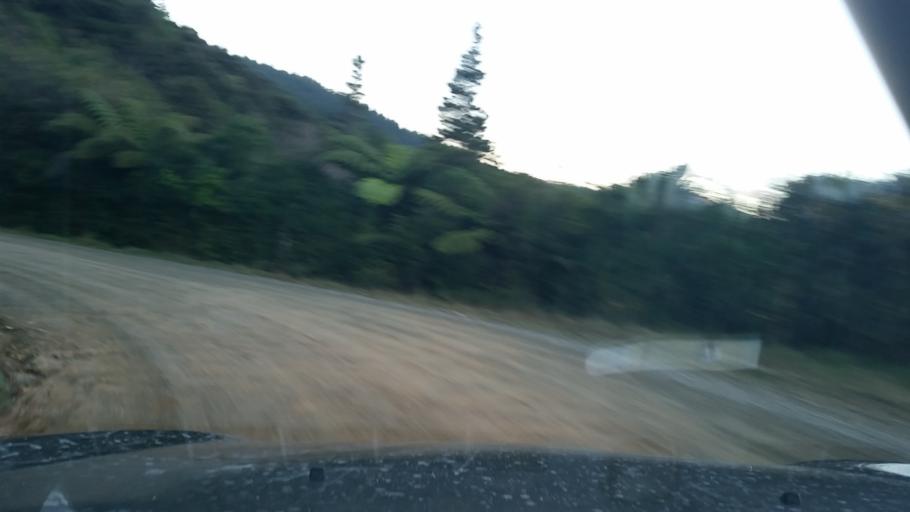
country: NZ
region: Marlborough
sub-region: Marlborough District
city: Picton
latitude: -41.1330
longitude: 174.1417
